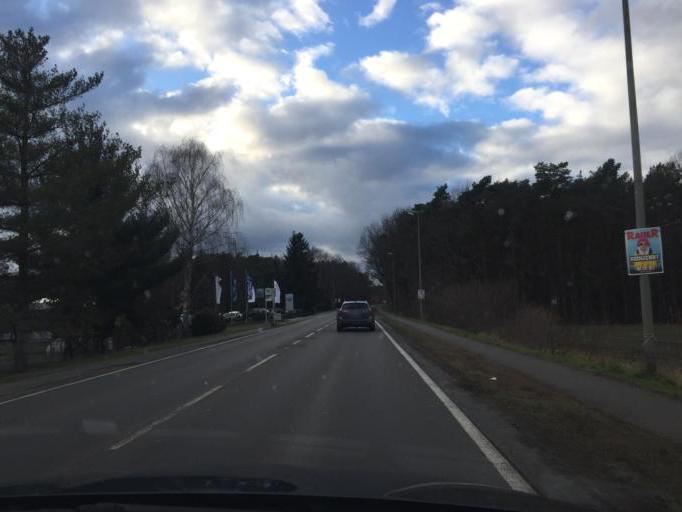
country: DE
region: Brandenburg
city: Kolkwitz
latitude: 51.7512
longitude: 14.2789
